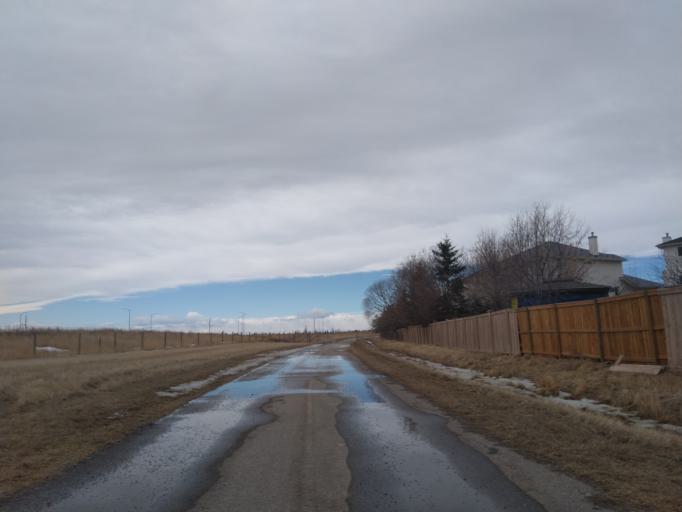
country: CA
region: Alberta
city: Chestermere
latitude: 51.0982
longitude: -113.9250
